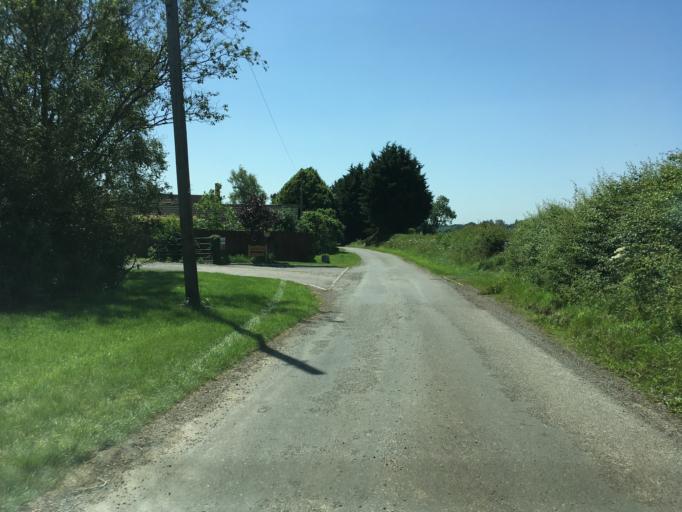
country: GB
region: England
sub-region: Northamptonshire
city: Brackley
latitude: 52.0151
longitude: -1.0718
